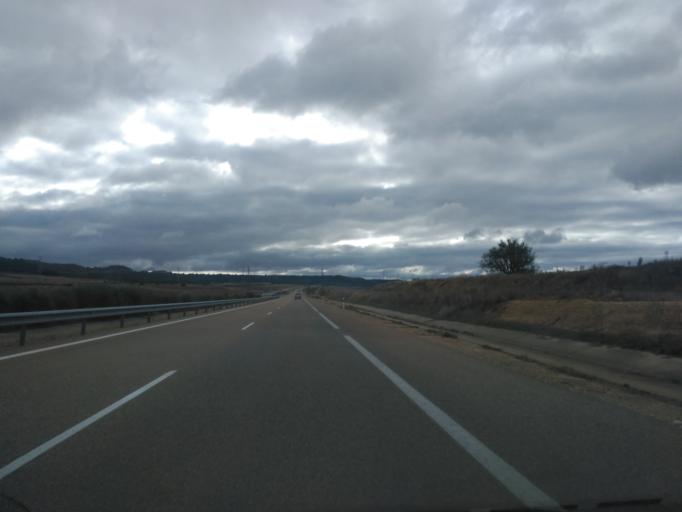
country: ES
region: Castille and Leon
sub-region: Provincia de Palencia
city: Villalobon
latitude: 42.0519
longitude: -4.4918
